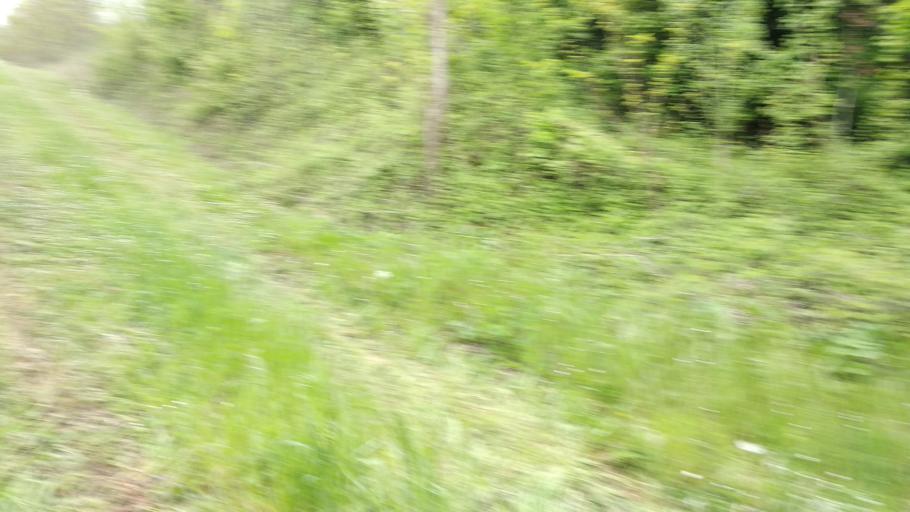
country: IT
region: Emilia-Romagna
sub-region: Forli-Cesena
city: Modigliana
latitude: 44.1410
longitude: 11.8015
